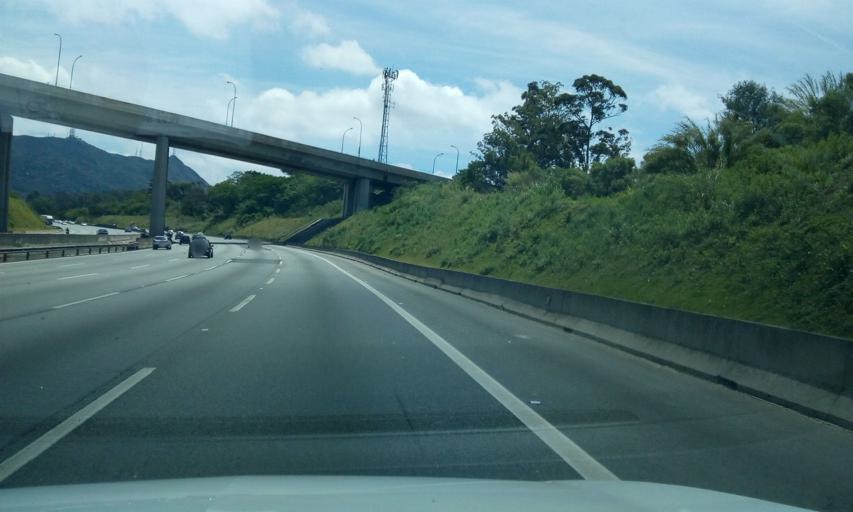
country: BR
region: Sao Paulo
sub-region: Osasco
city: Osasco
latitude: -23.4786
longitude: -46.7390
